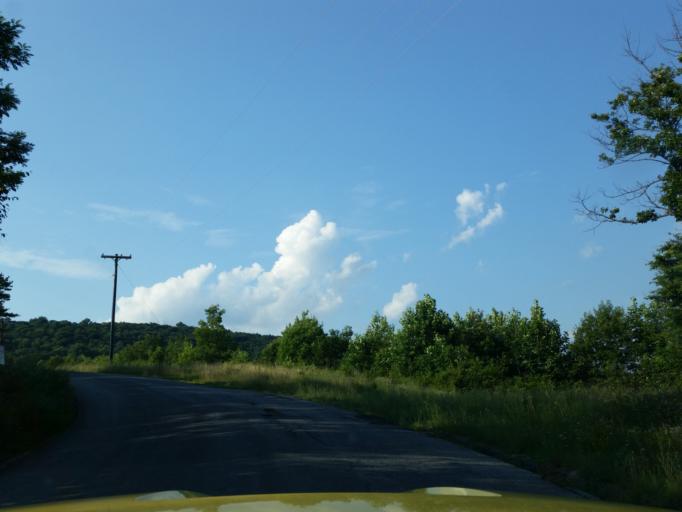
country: US
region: Pennsylvania
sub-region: Dauphin County
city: Williamstown
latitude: 40.4590
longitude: -76.6263
